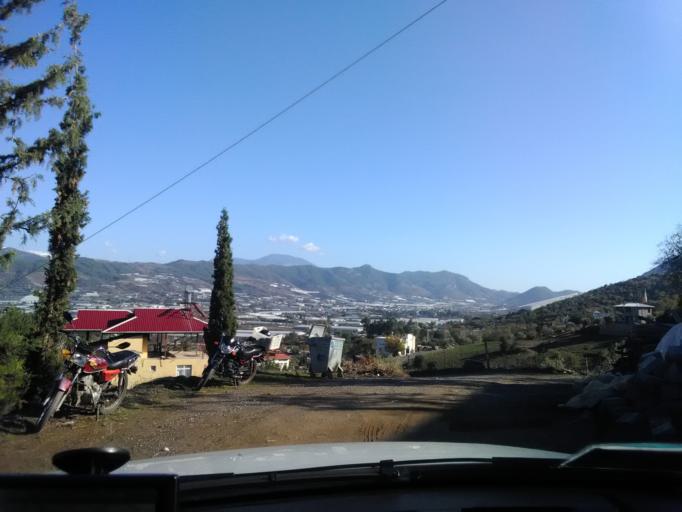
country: TR
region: Antalya
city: Gazipasa
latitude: 36.2499
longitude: 32.3340
